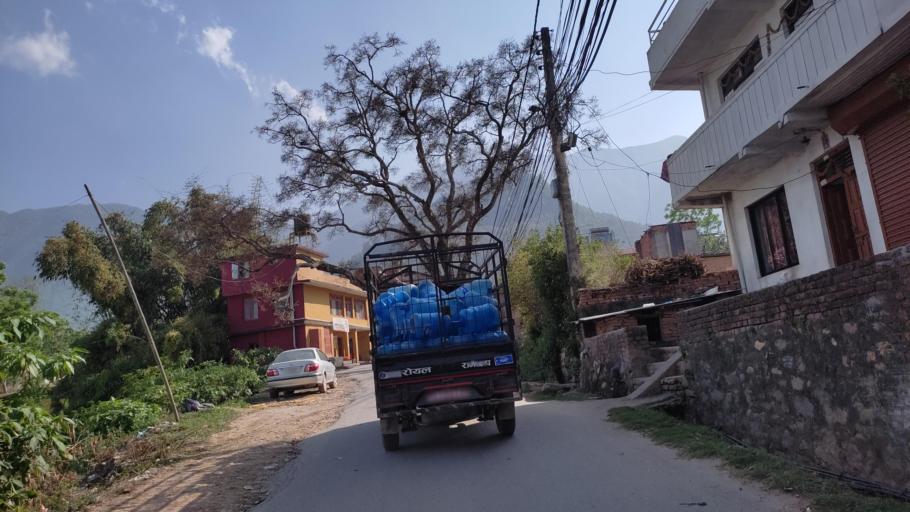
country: NP
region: Central Region
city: Kirtipur
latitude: 27.6724
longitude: 85.2512
